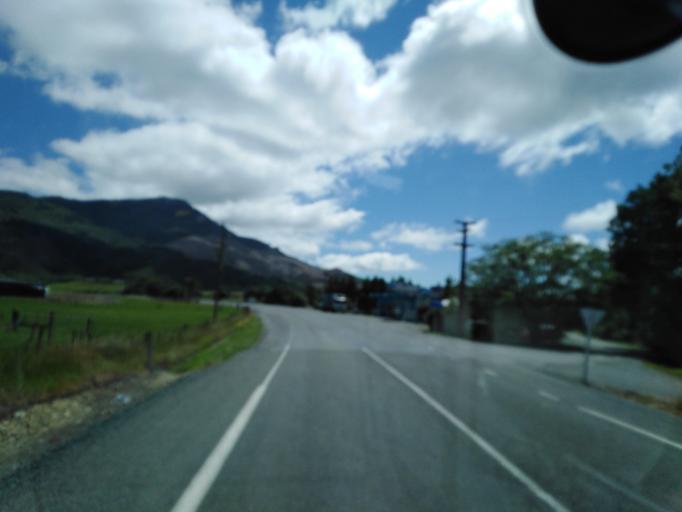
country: NZ
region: Nelson
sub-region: Nelson City
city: Nelson
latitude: -41.2141
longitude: 173.3955
